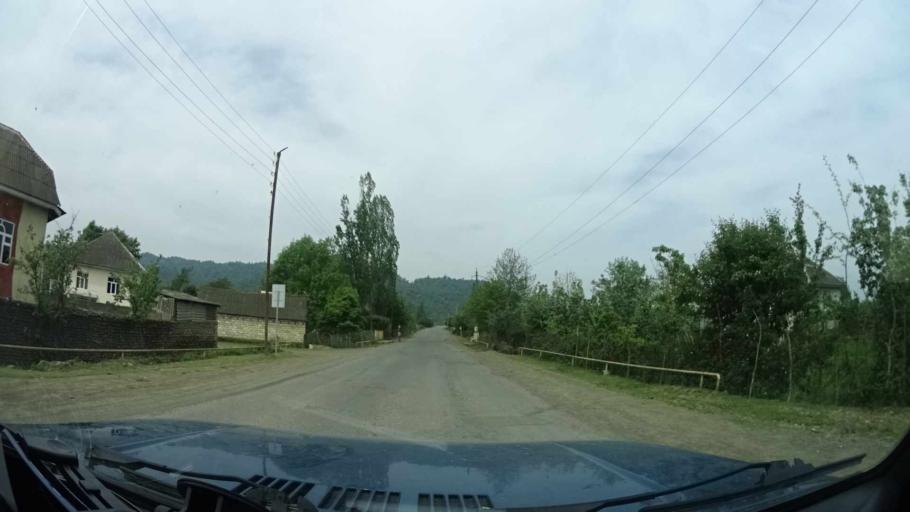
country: AZ
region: Lankaran
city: Haftoni
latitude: 38.7463
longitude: 48.7823
